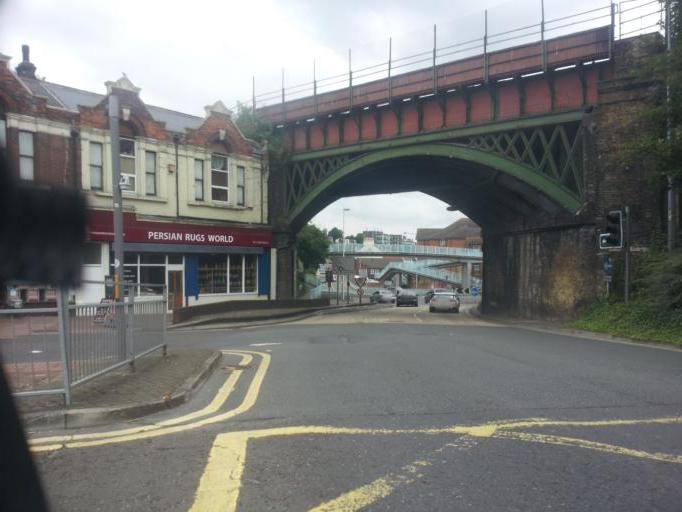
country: GB
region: England
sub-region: Kent
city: Chatham
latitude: 51.3785
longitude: 0.5348
